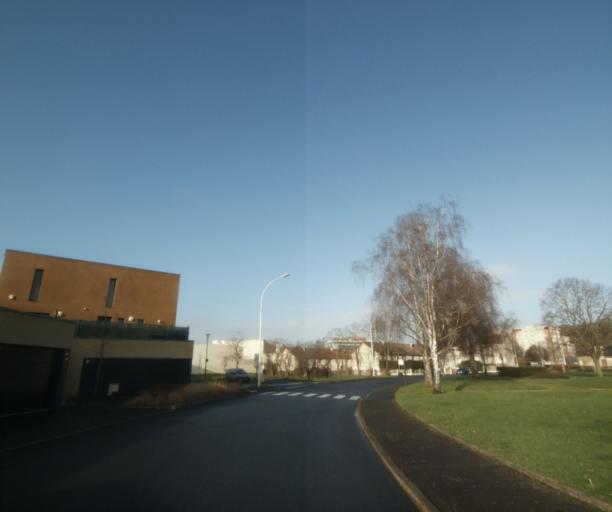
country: FR
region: Pays de la Loire
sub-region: Departement de la Sarthe
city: Le Mans
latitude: 47.9934
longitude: 0.2238
